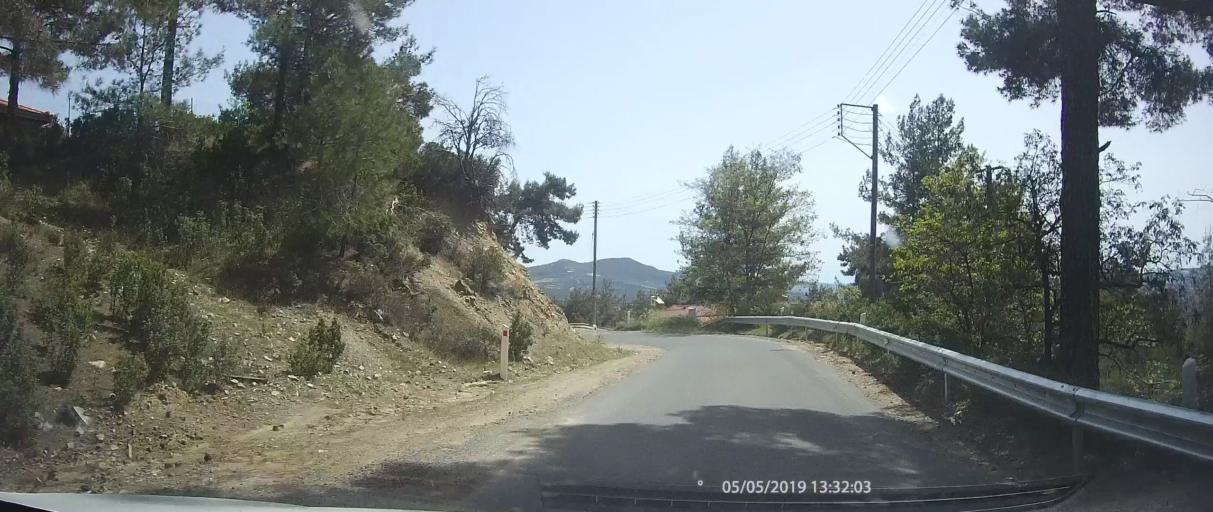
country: CY
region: Lefkosia
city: Kakopetria
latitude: 34.8904
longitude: 32.8518
